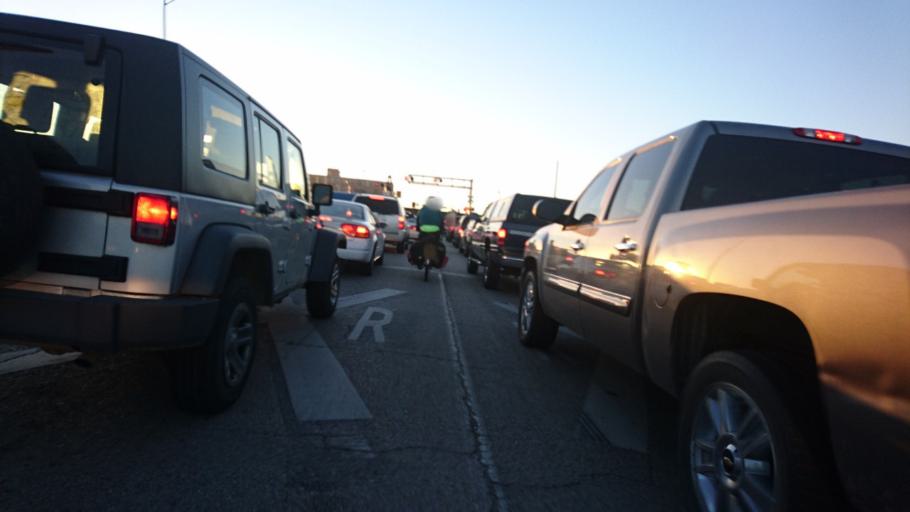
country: US
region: Oklahoma
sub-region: Rogers County
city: Claremore
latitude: 36.3135
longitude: -95.6184
